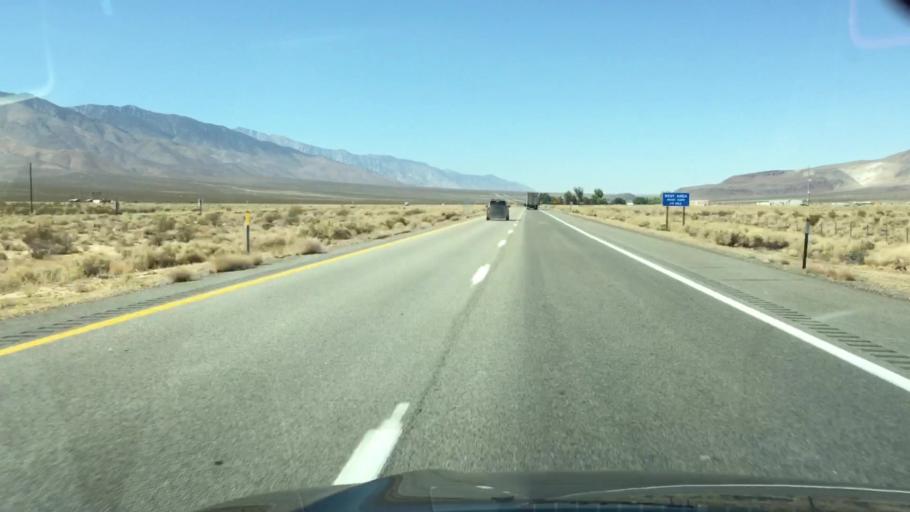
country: US
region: California
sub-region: Kern County
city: Inyokern
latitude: 36.0379
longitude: -117.9447
